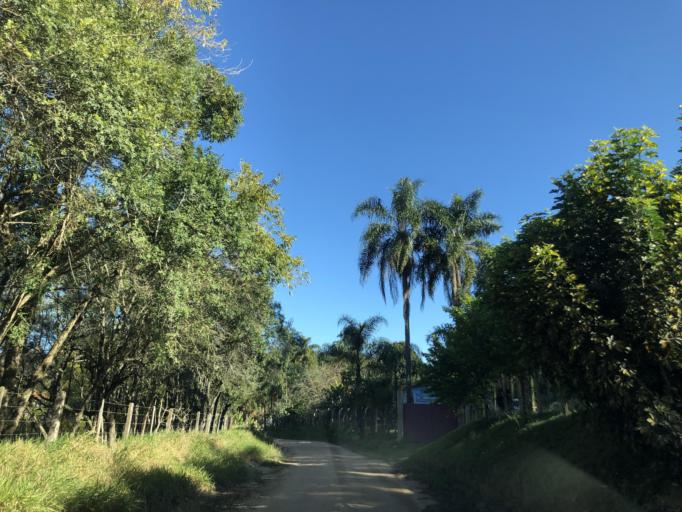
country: BR
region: Sao Paulo
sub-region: Pilar Do Sul
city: Pilar do Sul
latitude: -23.8203
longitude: -47.6316
